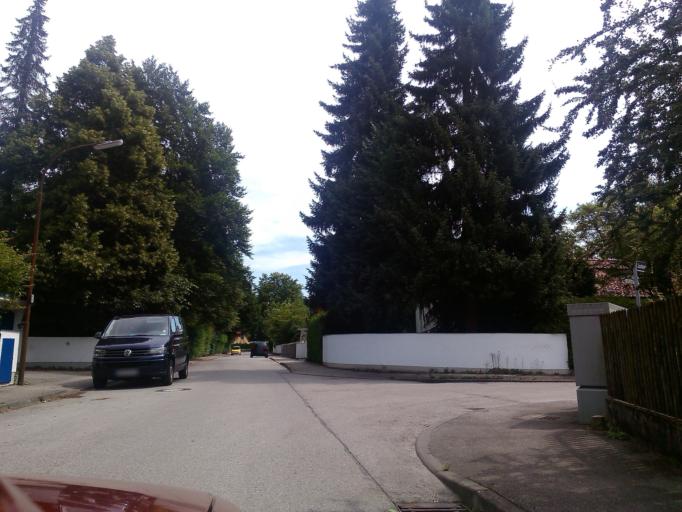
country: DE
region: Bavaria
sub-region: Upper Bavaria
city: Gauting
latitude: 48.0751
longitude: 11.3668
